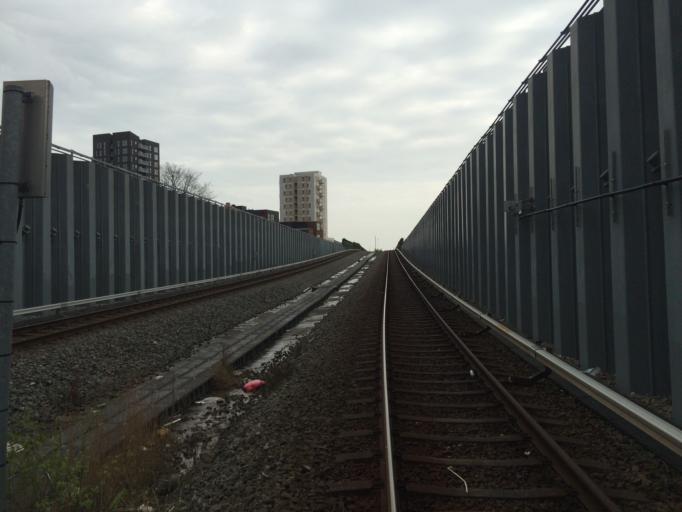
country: DK
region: Capital Region
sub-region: Kobenhavn
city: Christianshavn
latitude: 55.6608
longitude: 12.6291
